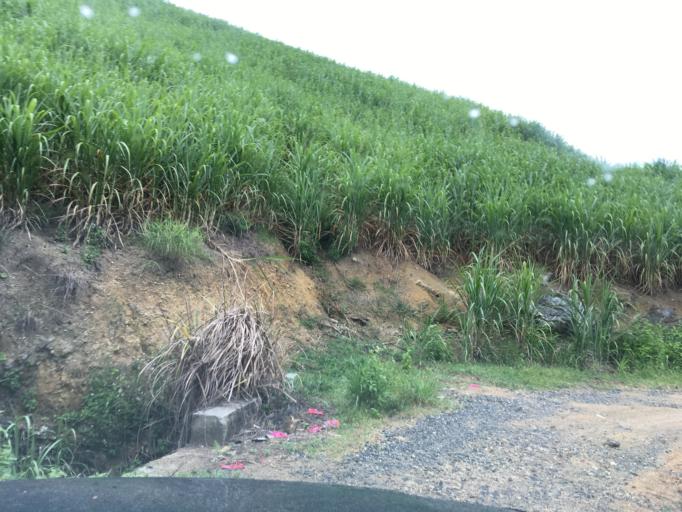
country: CN
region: Guangxi Zhuangzu Zizhiqu
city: Tongle
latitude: 25.0033
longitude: 105.9932
